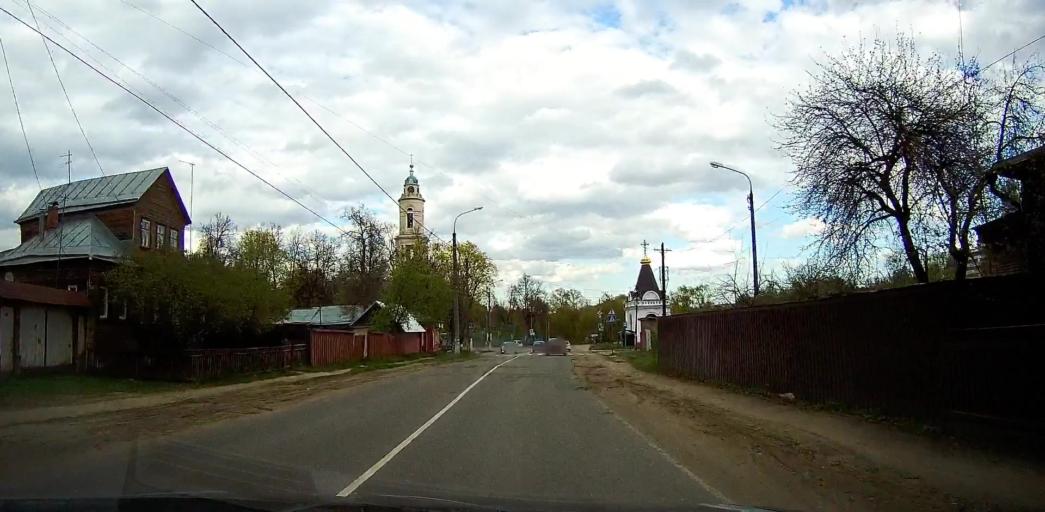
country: RU
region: Moskovskaya
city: Pavlovskiy Posad
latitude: 55.7834
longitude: 38.6477
